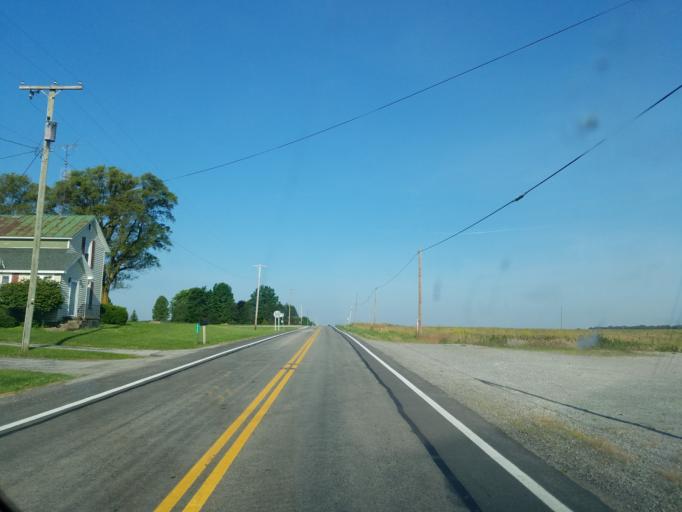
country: US
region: Ohio
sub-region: Hardin County
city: Kenton
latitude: 40.7319
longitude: -83.6450
